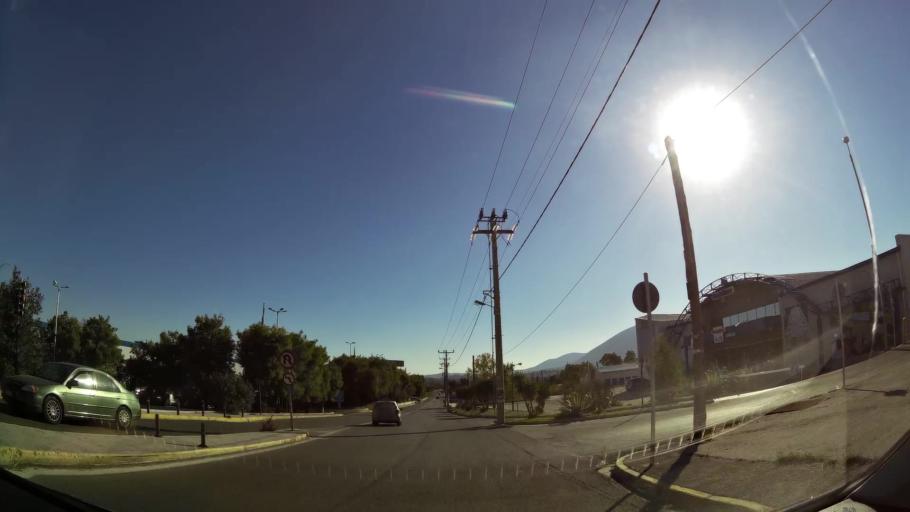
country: GR
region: Attica
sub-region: Nomarchia Anatolikis Attikis
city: Anthousa
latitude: 38.0156
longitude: 23.8718
